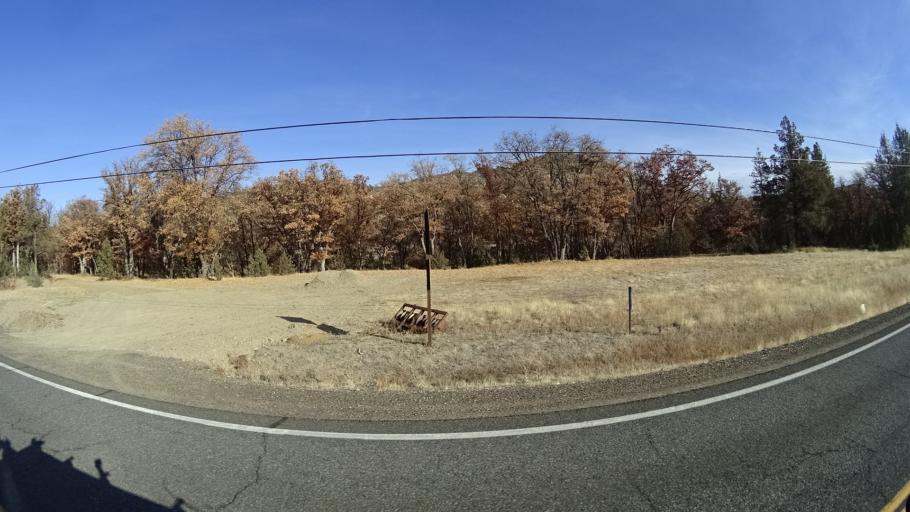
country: US
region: California
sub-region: Siskiyou County
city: Yreka
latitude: 41.6598
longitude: -122.5947
